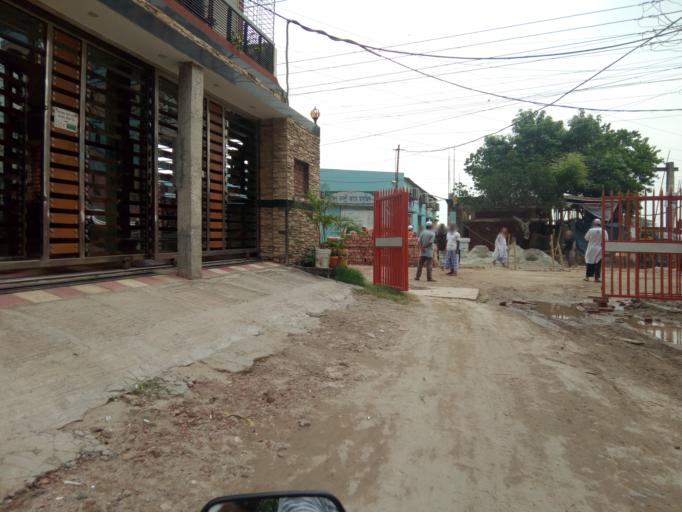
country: BD
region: Dhaka
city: Paltan
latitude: 23.7567
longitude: 90.4435
